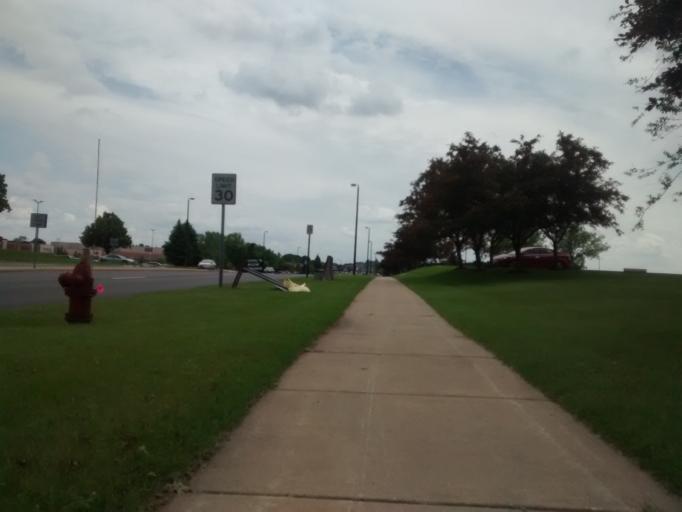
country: US
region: Minnesota
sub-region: Dakota County
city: Burnsville
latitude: 44.7518
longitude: -93.2882
